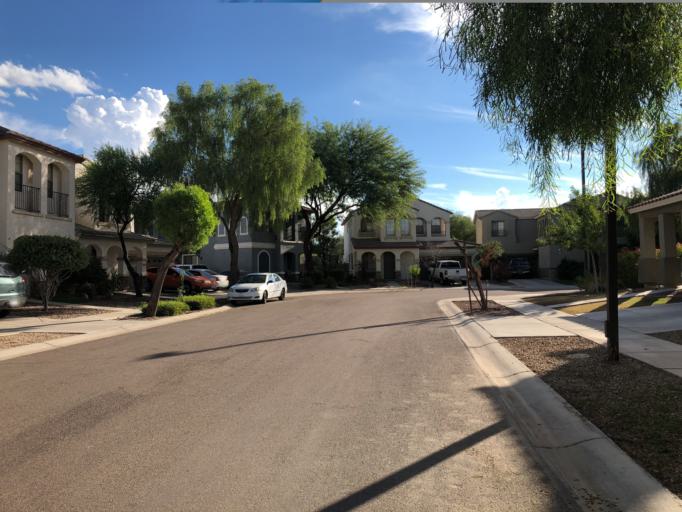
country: US
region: Arizona
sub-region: Maricopa County
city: Queen Creek
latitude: 33.2767
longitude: -111.7111
